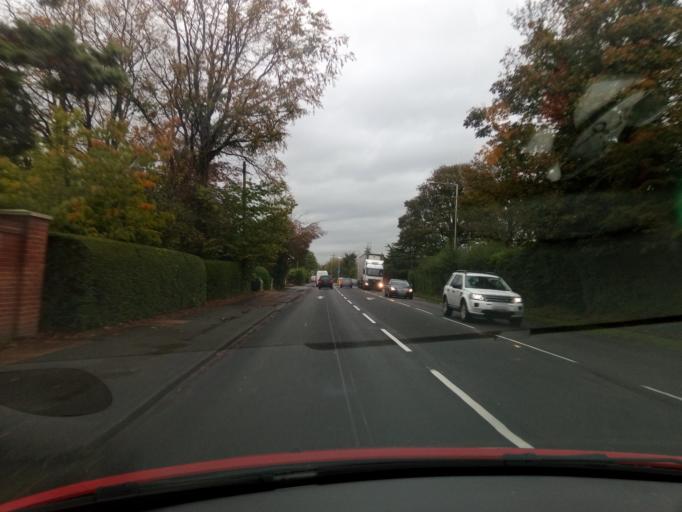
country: GB
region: England
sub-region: Lancashire
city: Catterall
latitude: 53.8321
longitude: -2.7382
